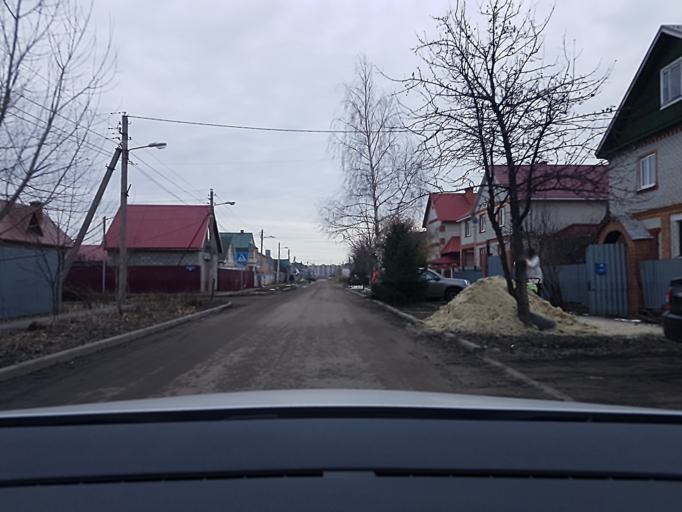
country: RU
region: Tambov
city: Tambov
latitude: 52.7797
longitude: 41.3802
